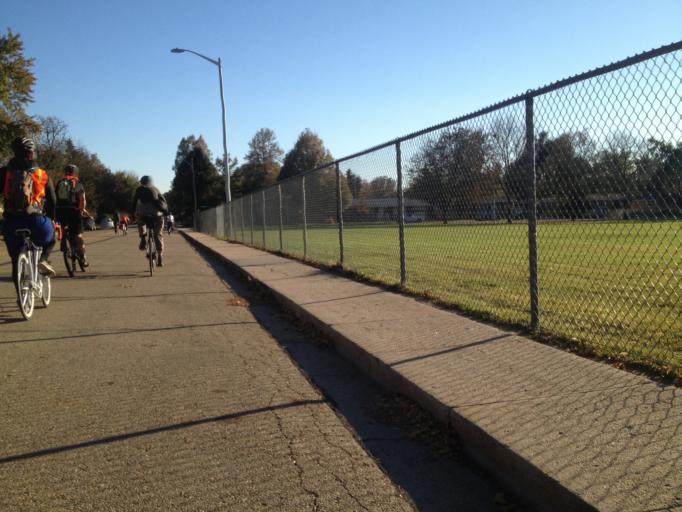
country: US
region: Colorado
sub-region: Boulder County
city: Longmont
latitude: 40.1829
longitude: -105.1145
